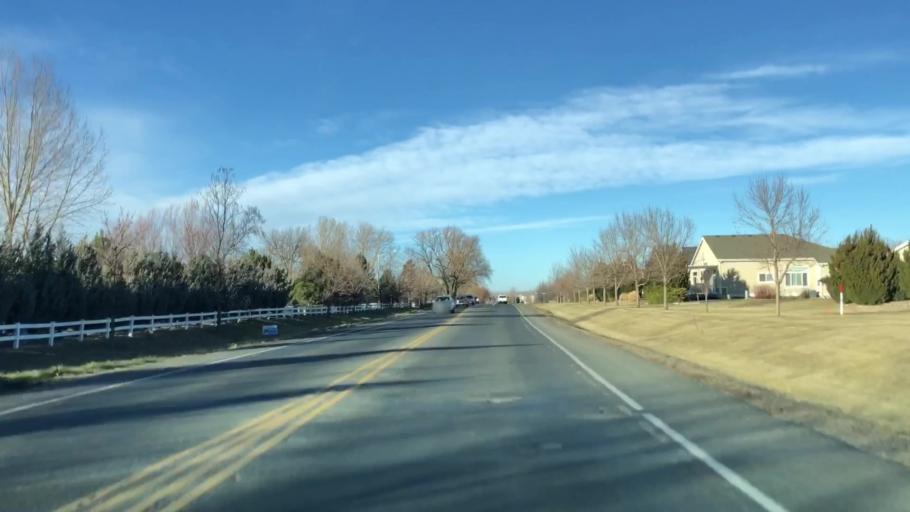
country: US
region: Colorado
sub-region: Weld County
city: Windsor
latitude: 40.4683
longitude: -104.9822
